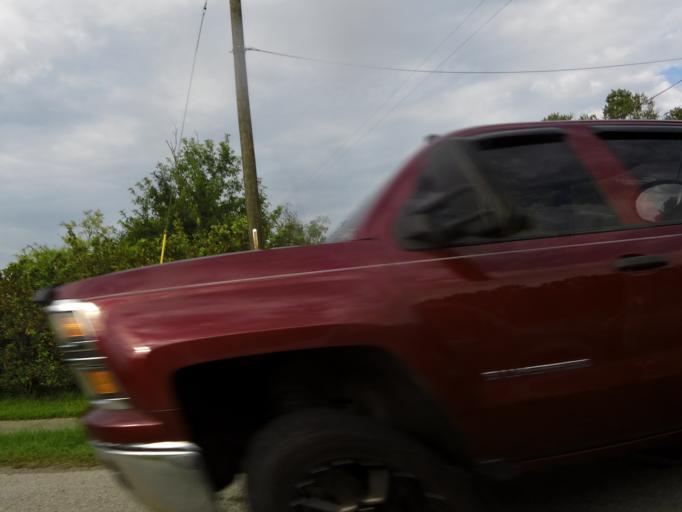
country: US
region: Florida
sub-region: Nassau County
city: Nassau Village-Ratliff
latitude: 30.4279
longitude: -81.7635
